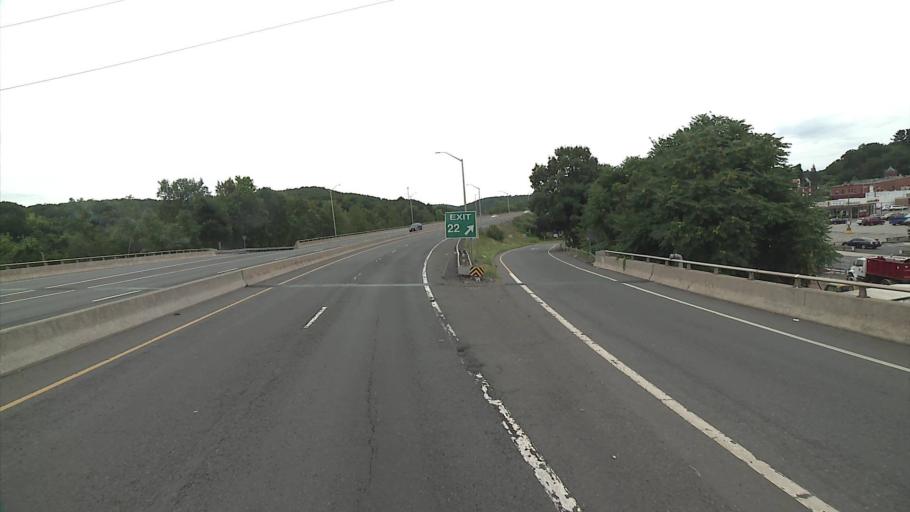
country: US
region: Connecticut
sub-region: New Haven County
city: Seymour
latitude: 41.3945
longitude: -73.0758
